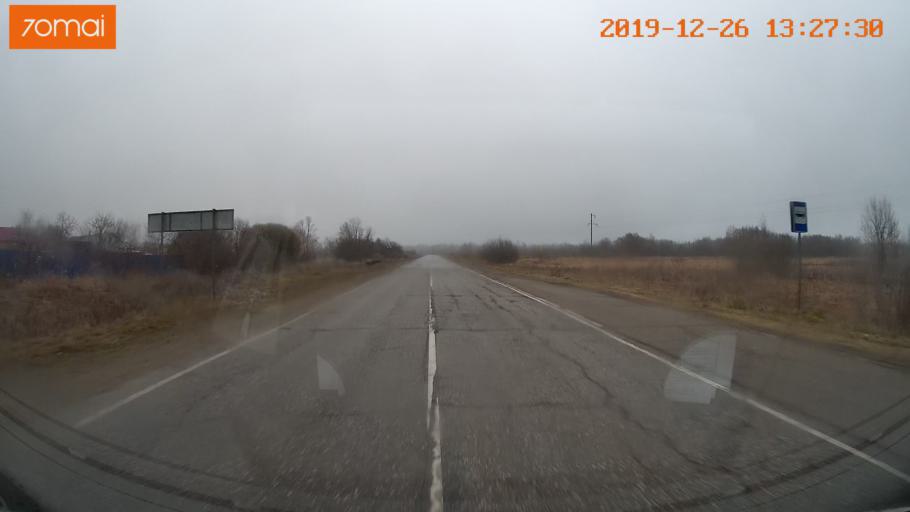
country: RU
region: Vologda
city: Cherepovets
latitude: 58.8533
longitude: 38.2405
